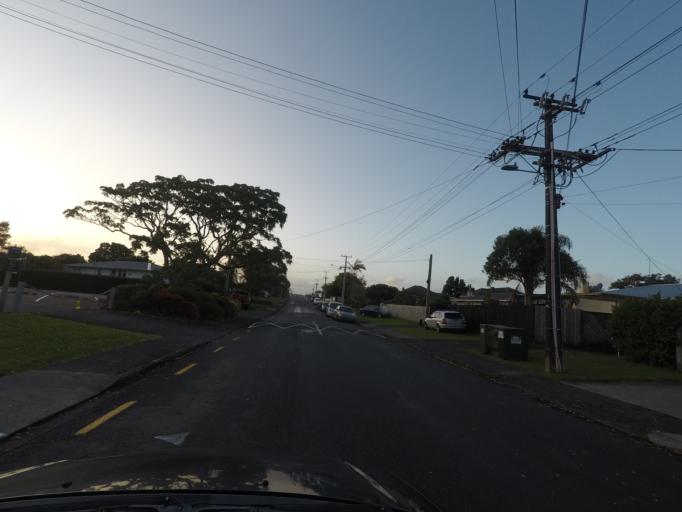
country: NZ
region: Auckland
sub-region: Auckland
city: Rosebank
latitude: -36.8386
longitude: 174.6466
